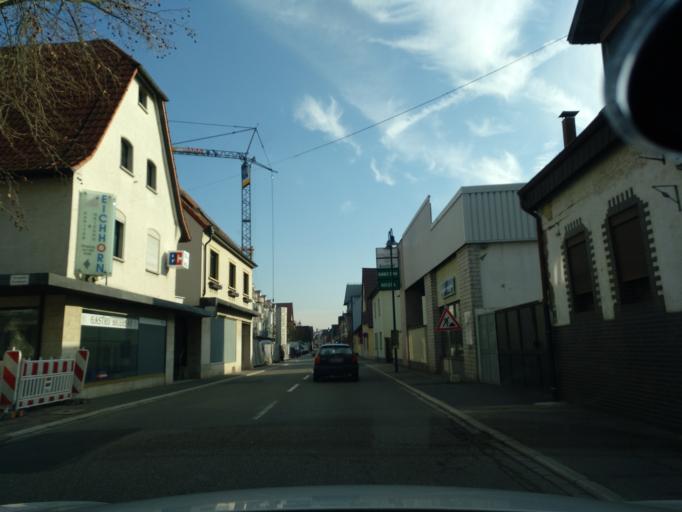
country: DE
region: Baden-Wuerttemberg
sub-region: Karlsruhe Region
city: Hockenheim
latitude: 49.3166
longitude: 8.5491
